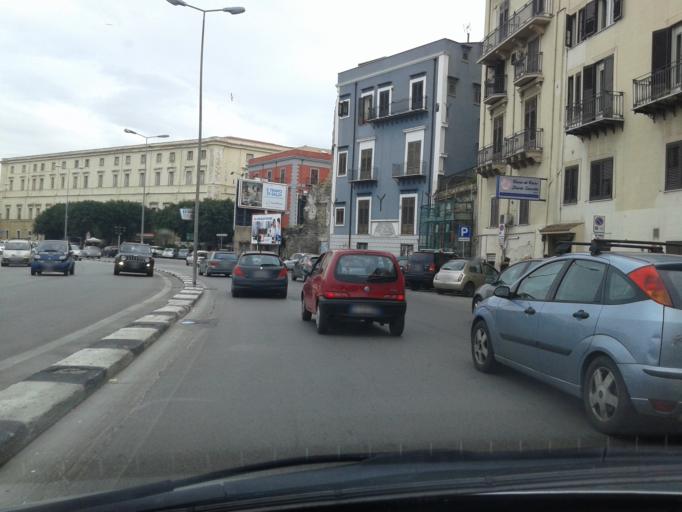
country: IT
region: Sicily
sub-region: Palermo
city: Palermo
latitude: 38.1197
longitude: 13.3666
